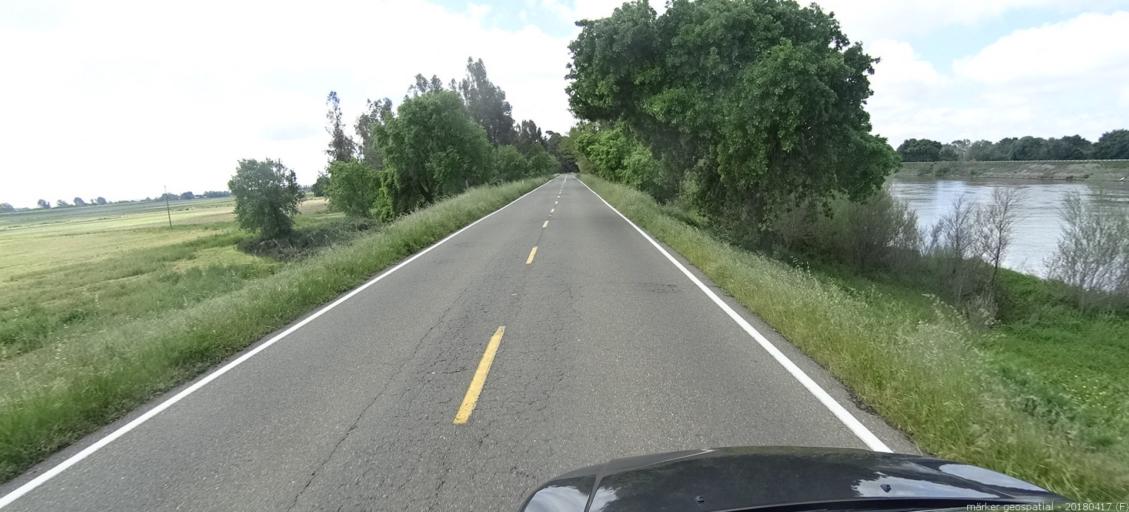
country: US
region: California
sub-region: Sacramento County
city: Walnut Grove
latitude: 38.1801
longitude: -121.5868
